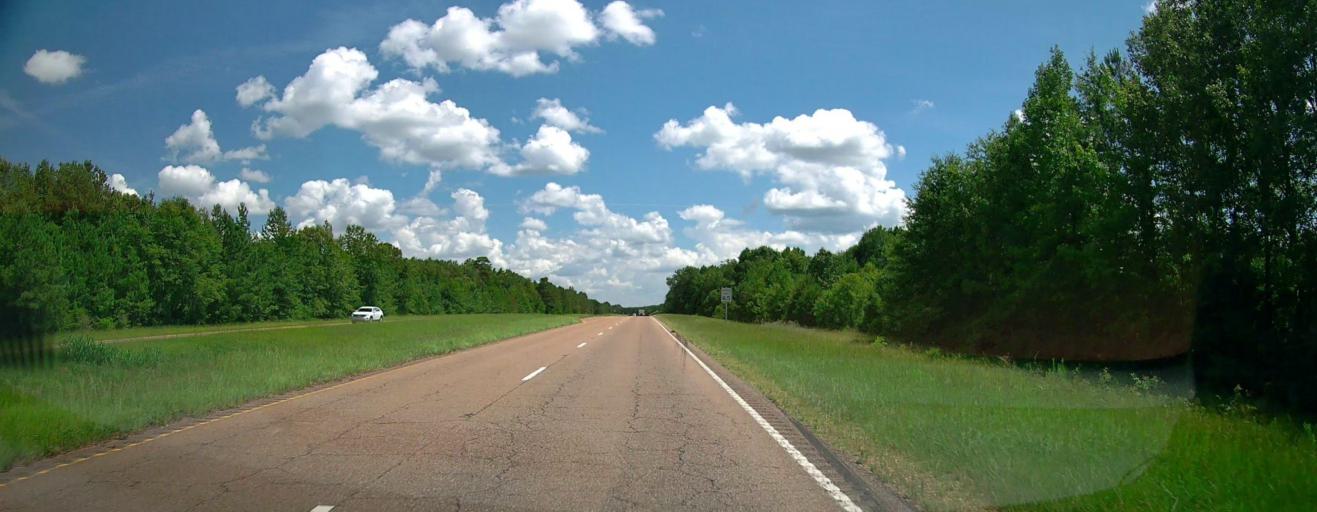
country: US
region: Mississippi
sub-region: Monroe County
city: Aberdeen
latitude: 33.8323
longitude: -88.5881
